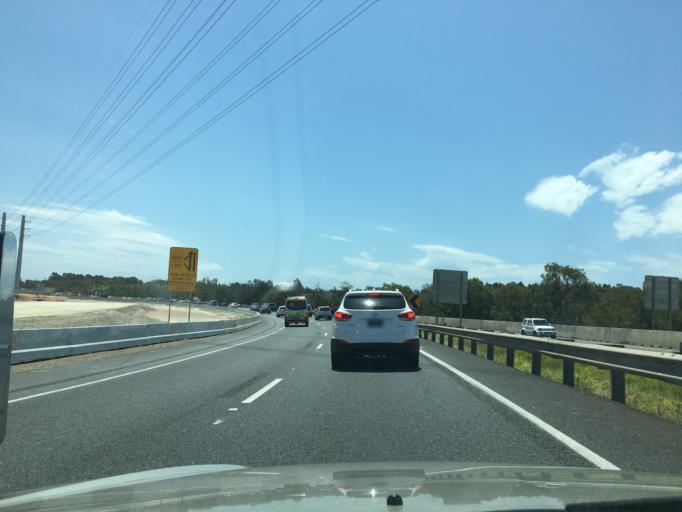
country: AU
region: Queensland
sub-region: Brisbane
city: Shorncliffe
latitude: -27.3667
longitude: 153.0977
